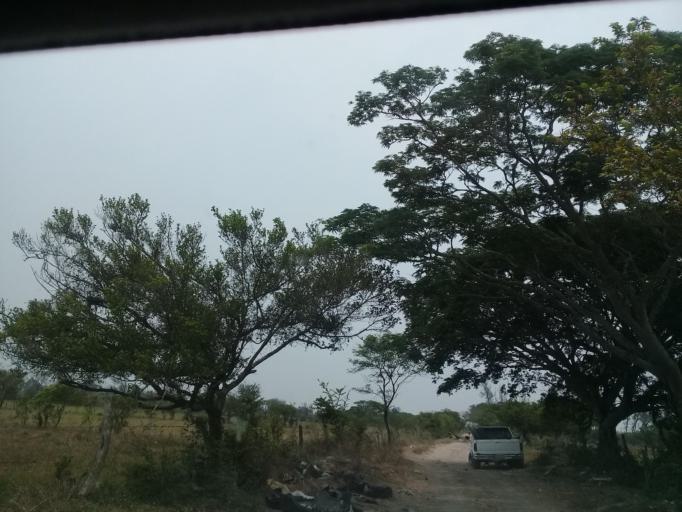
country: MX
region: Veracruz
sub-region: Veracruz
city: Las Amapolas
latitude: 19.1447
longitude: -96.2087
